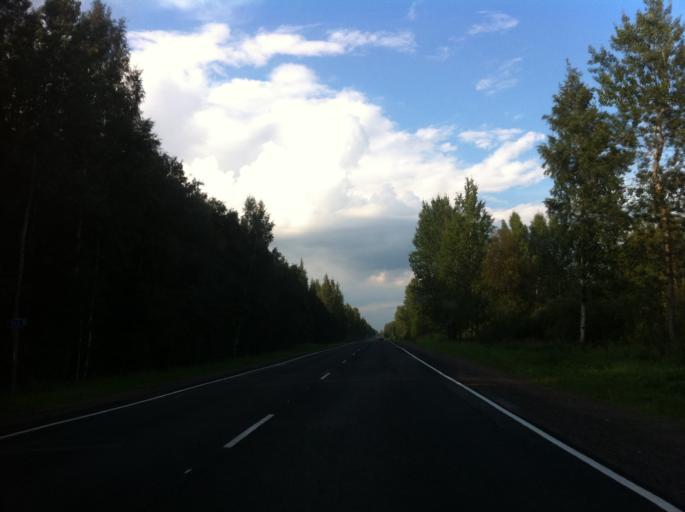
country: RU
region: Leningrad
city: Luga
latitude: 58.4963
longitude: 29.7848
